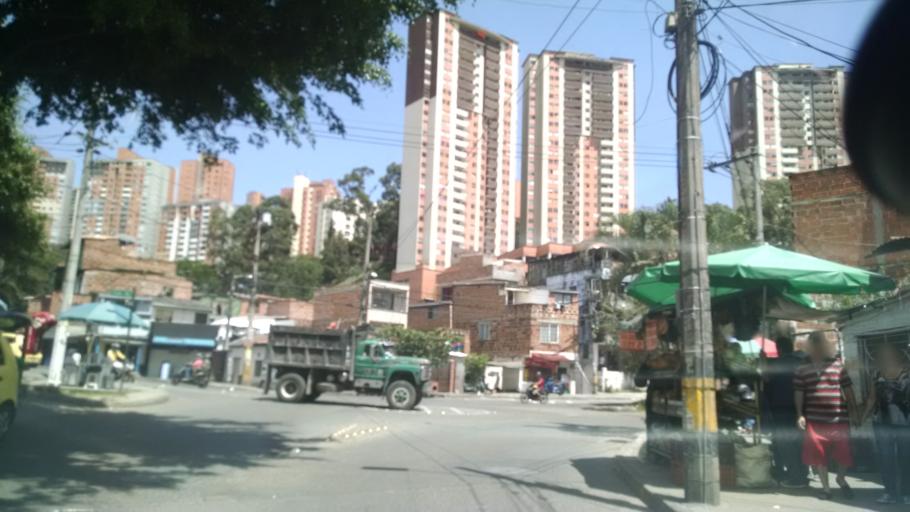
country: CO
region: Antioquia
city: Itagui
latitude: 6.2144
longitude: -75.6020
